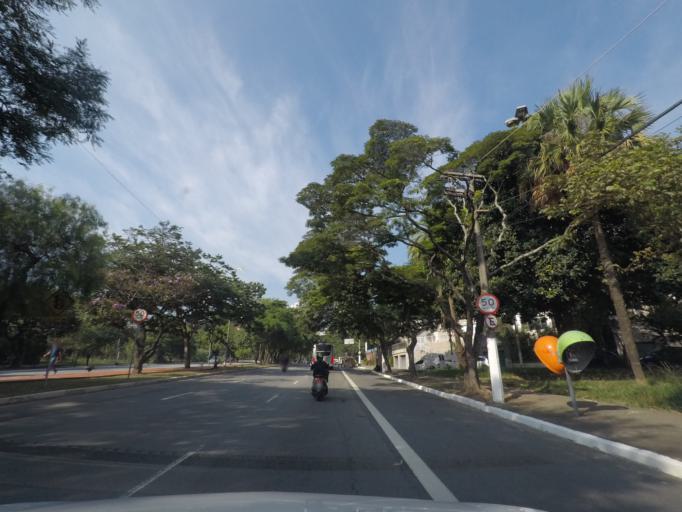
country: BR
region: Sao Paulo
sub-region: Sao Paulo
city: Sao Paulo
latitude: -23.5485
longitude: -46.6773
